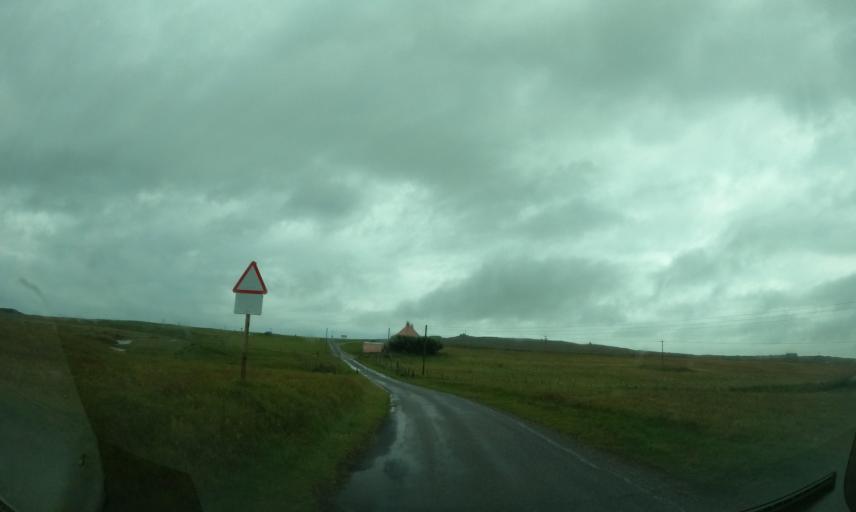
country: GB
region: Scotland
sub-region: Eilean Siar
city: Barra
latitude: 56.5146
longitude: -6.8162
